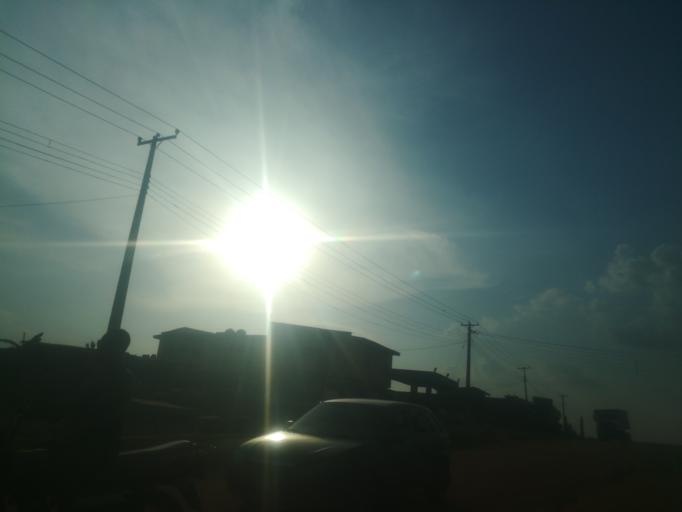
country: NG
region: Ogun
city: Abeokuta
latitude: 7.1667
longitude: 3.3035
